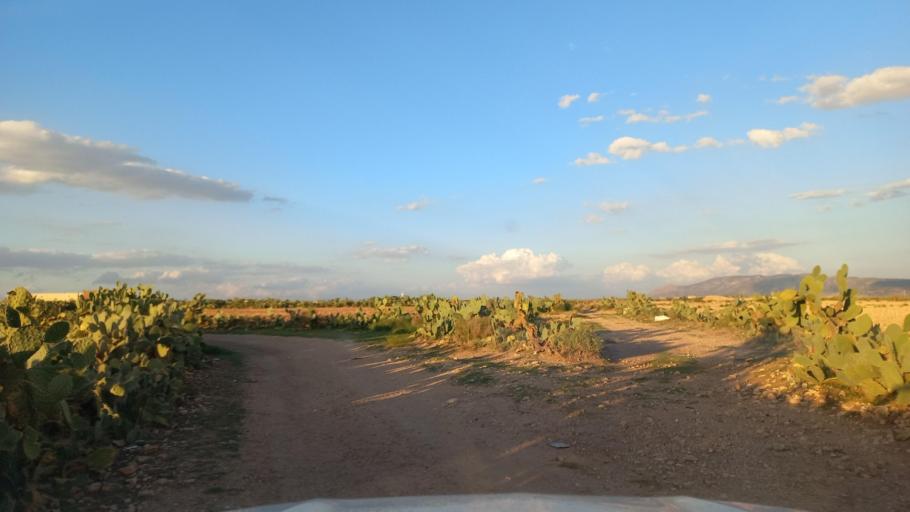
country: TN
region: Al Qasrayn
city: Sbiba
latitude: 35.3734
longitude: 9.0555
